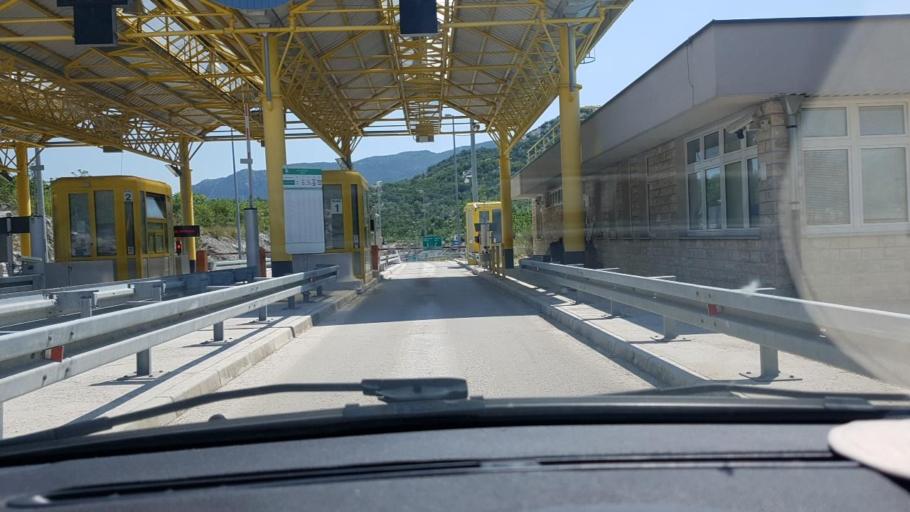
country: HR
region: Splitsko-Dalmatinska
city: Vrgorac
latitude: 43.1919
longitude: 17.3789
